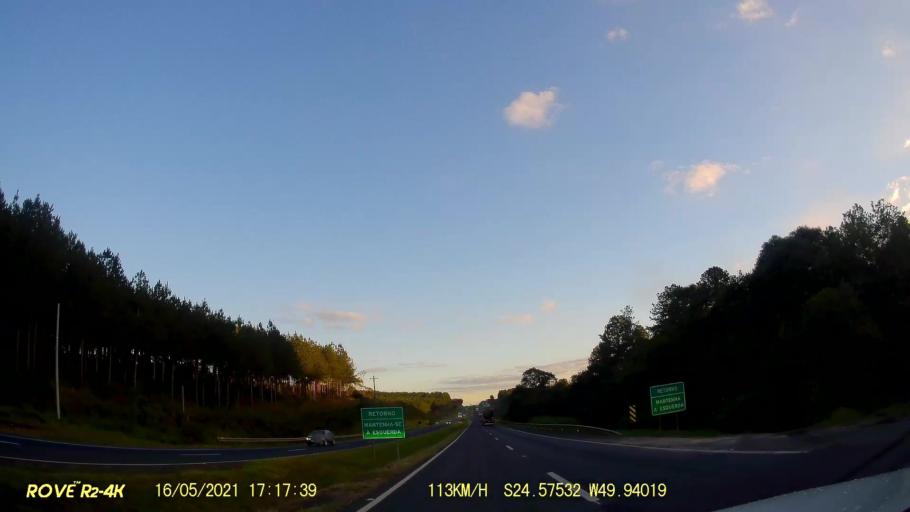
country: BR
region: Parana
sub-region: Pirai Do Sul
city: Pirai do Sul
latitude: -24.5757
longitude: -49.9403
